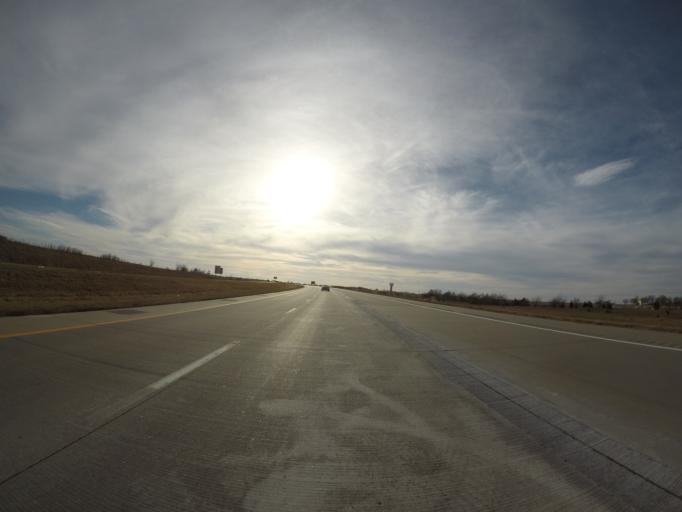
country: US
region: Kansas
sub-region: Franklin County
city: Ottawa
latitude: 38.6364
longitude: -95.2263
